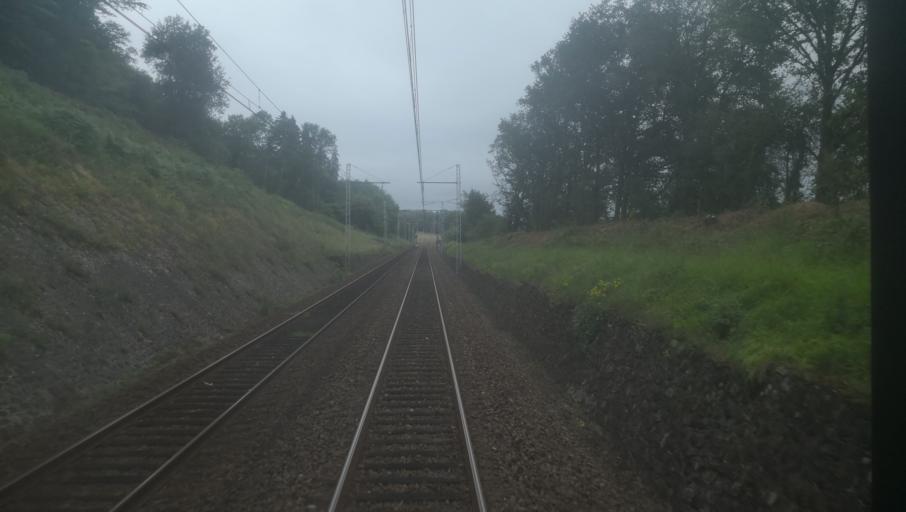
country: FR
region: Centre
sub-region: Departement de l'Indre
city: Le Pechereau
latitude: 46.5640
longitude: 1.5267
